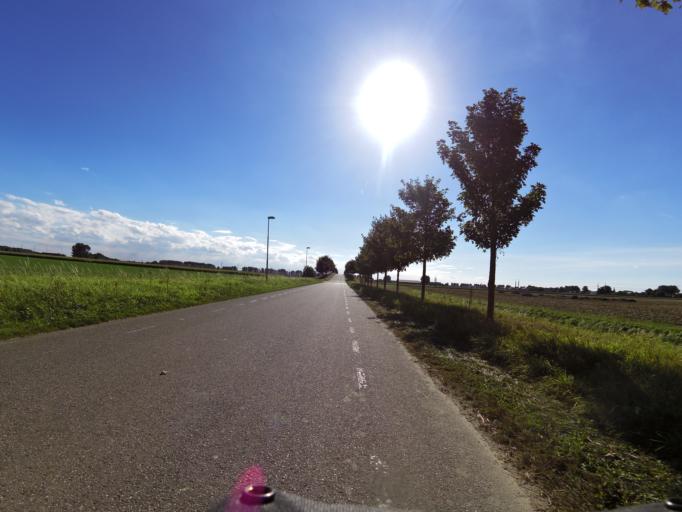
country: NL
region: South Holland
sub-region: Gemeente Zwijndrecht
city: Zwijndrecht
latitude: 51.7465
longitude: 4.6235
